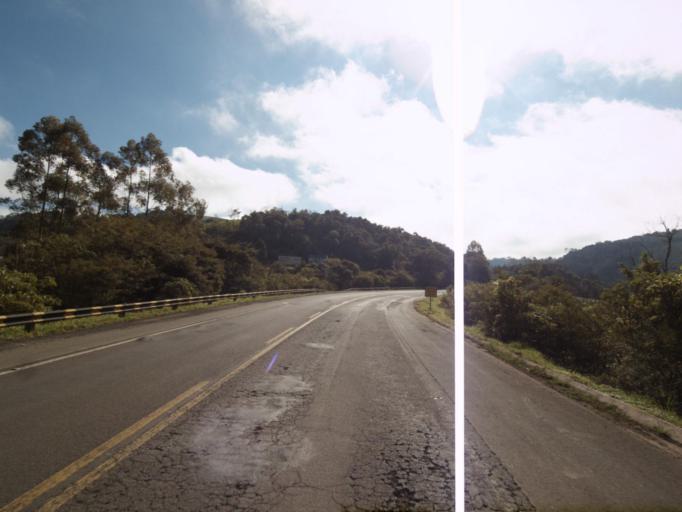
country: BR
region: Rio Grande do Sul
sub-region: Frederico Westphalen
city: Frederico Westphalen
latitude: -27.1380
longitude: -53.2143
